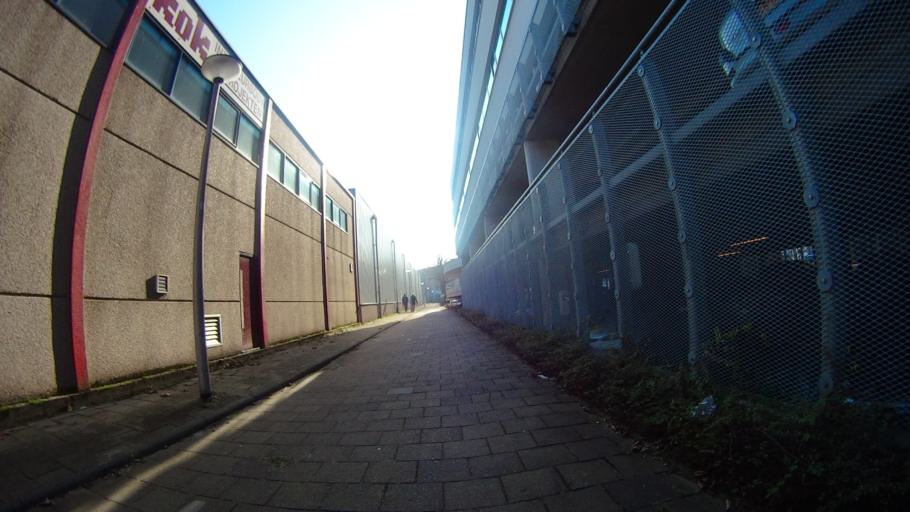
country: NL
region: Utrecht
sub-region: Gemeente Amersfoort
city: Randenbroek
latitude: 52.1760
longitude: 5.4140
